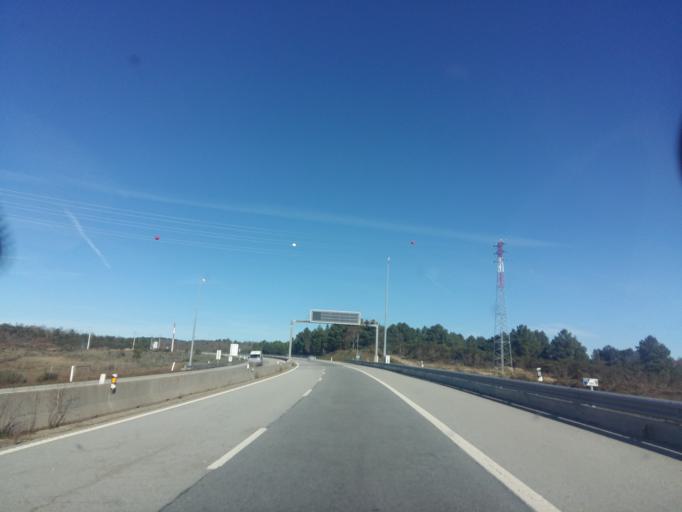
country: PT
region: Guarda
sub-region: Guarda
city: Sequeira
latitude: 40.5299
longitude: -7.2190
